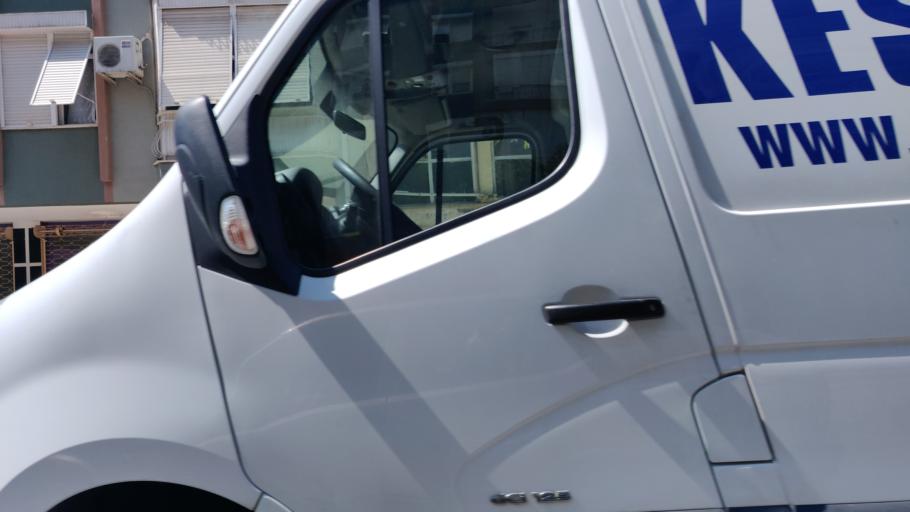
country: TR
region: Antalya
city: Antalya
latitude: 36.9088
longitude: 30.6835
